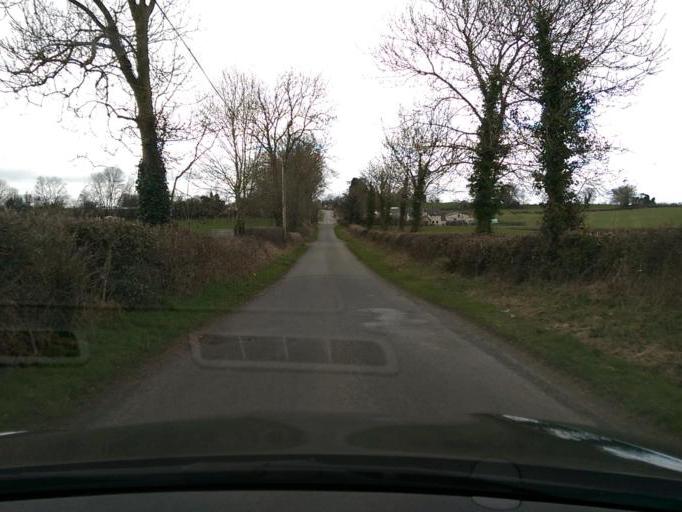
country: IE
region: Leinster
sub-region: Uibh Fhaili
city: Clara
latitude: 53.4002
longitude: -7.6203
